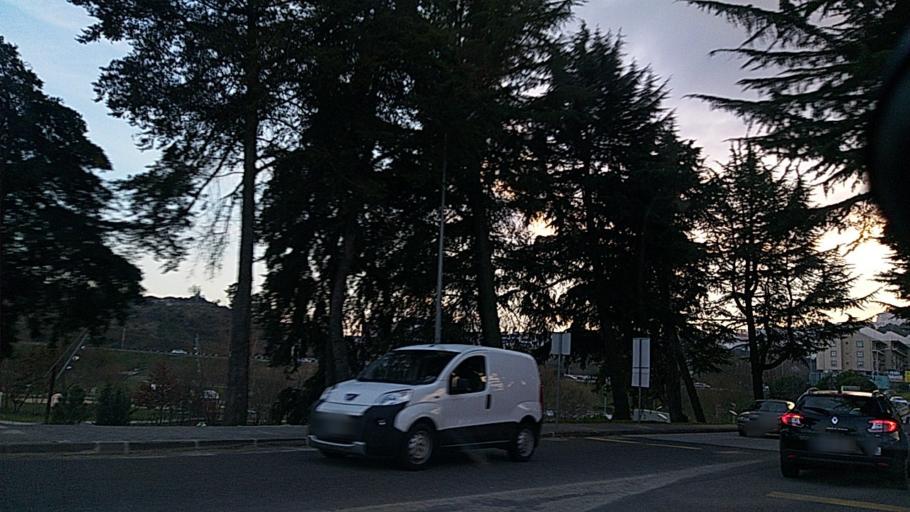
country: PT
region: Guarda
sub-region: Guarda
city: Sequeira
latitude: 40.5499
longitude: -7.2467
